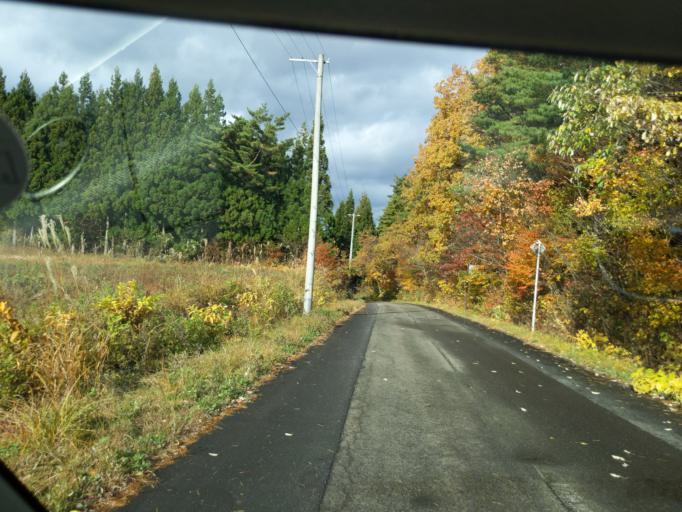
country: JP
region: Iwate
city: Mizusawa
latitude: 39.1111
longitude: 140.9731
